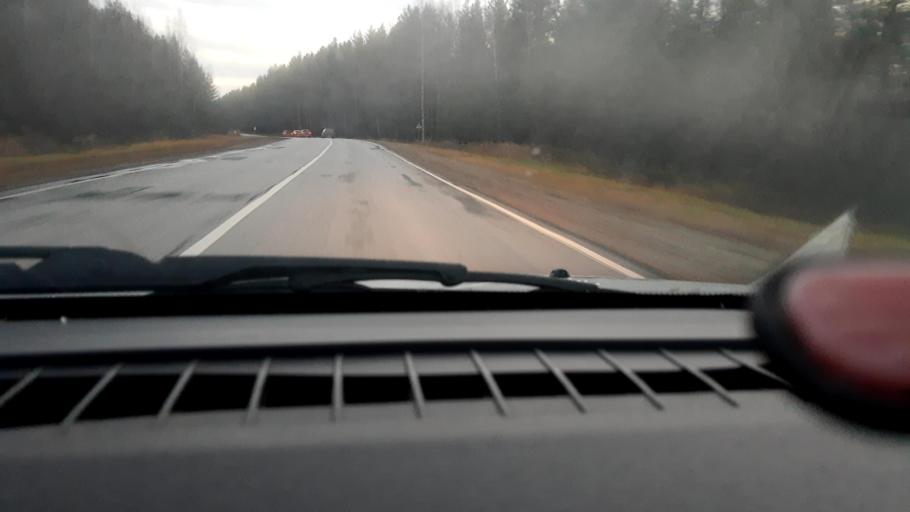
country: RU
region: Nizjnij Novgorod
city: Krasnyye Baki
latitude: 57.0062
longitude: 45.1118
